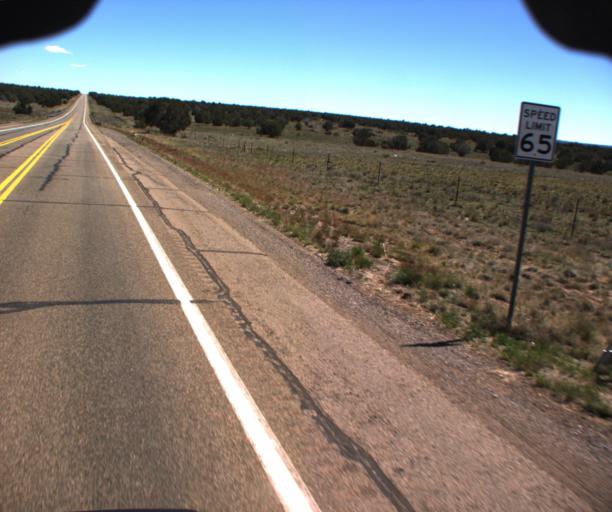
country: US
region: Arizona
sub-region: Coconino County
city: Williams
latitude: 35.1892
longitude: -112.4691
